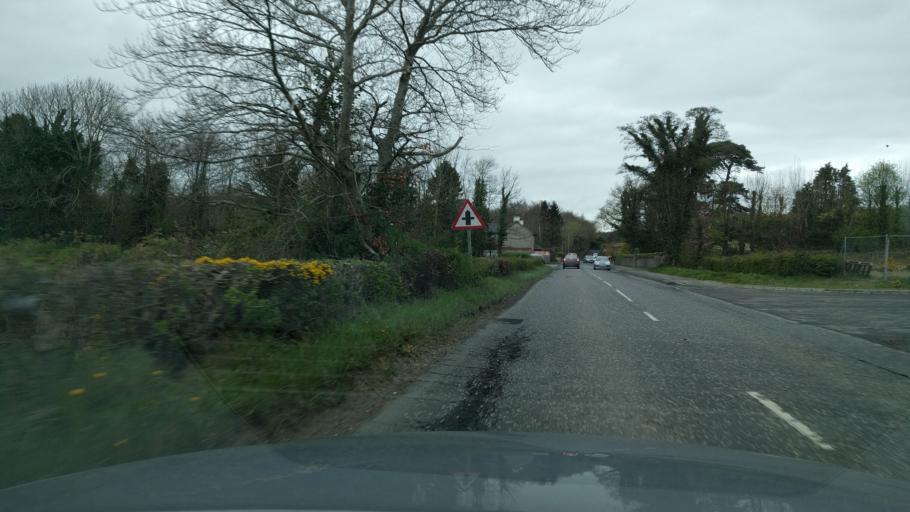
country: GB
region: Northern Ireland
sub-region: Down District
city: Warrenpoint
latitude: 54.1190
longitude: -6.2677
